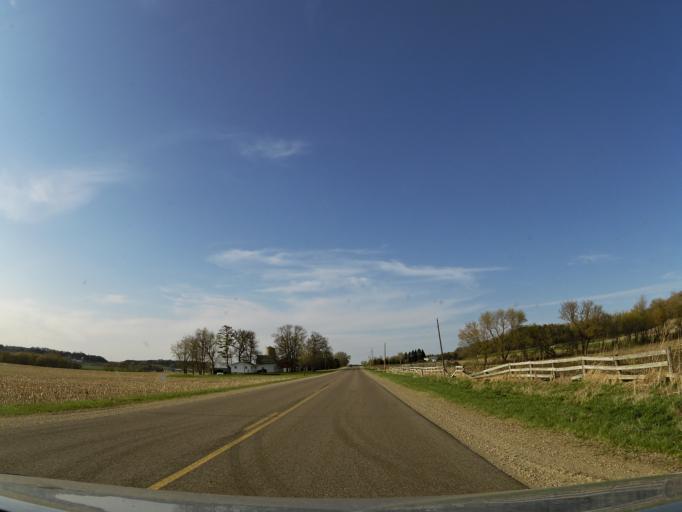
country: US
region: Wisconsin
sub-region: Pierce County
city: River Falls
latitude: 44.8035
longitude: -92.6449
